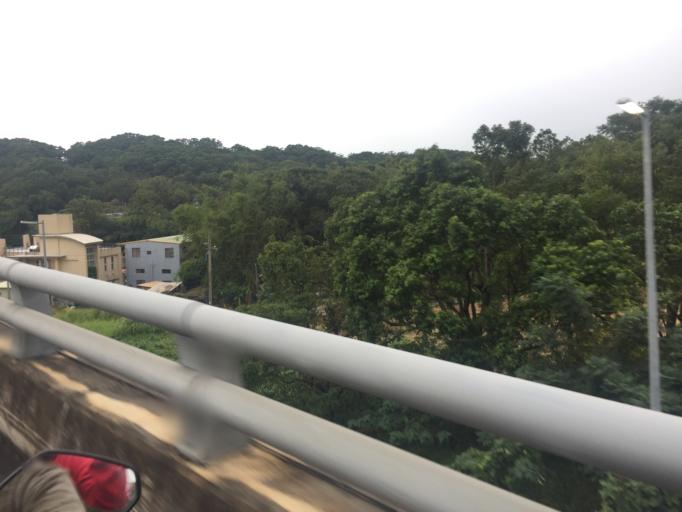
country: TW
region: Taiwan
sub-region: Hsinchu
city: Hsinchu
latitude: 24.7737
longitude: 120.9530
